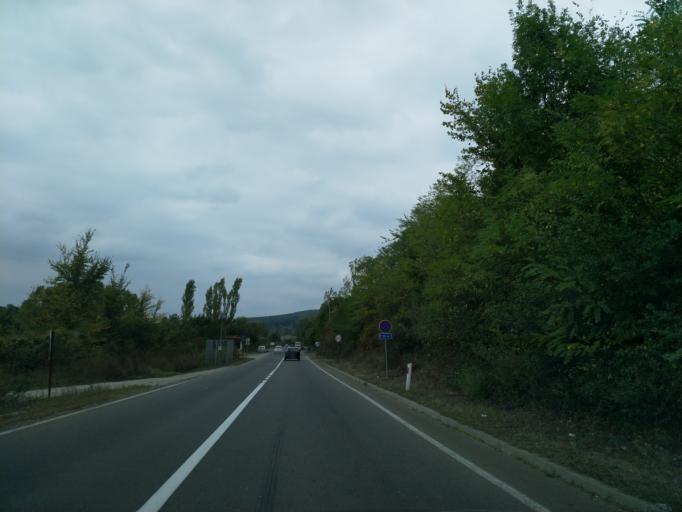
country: RS
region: Central Serbia
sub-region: Sumadijski Okrug
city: Topola
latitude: 44.2136
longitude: 20.7236
